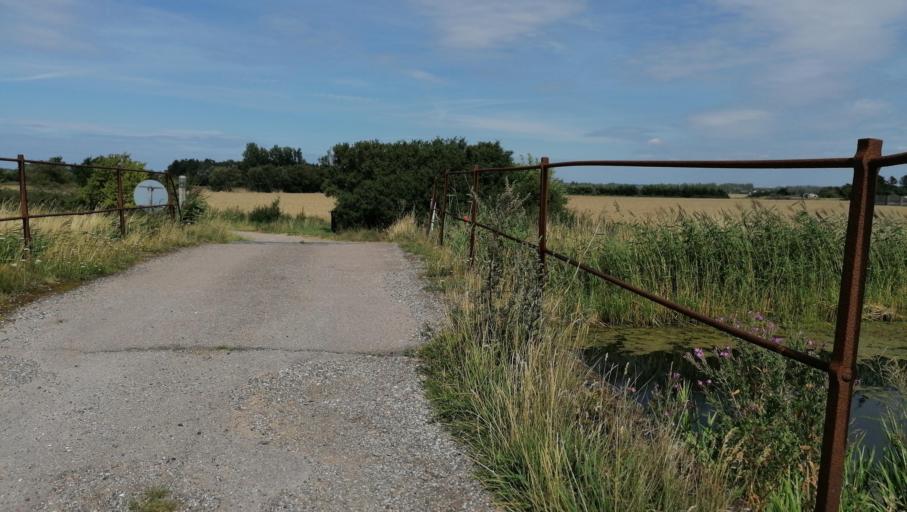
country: DK
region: Zealand
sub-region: Odsherred Kommune
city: Horve
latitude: 55.7691
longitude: 11.4615
